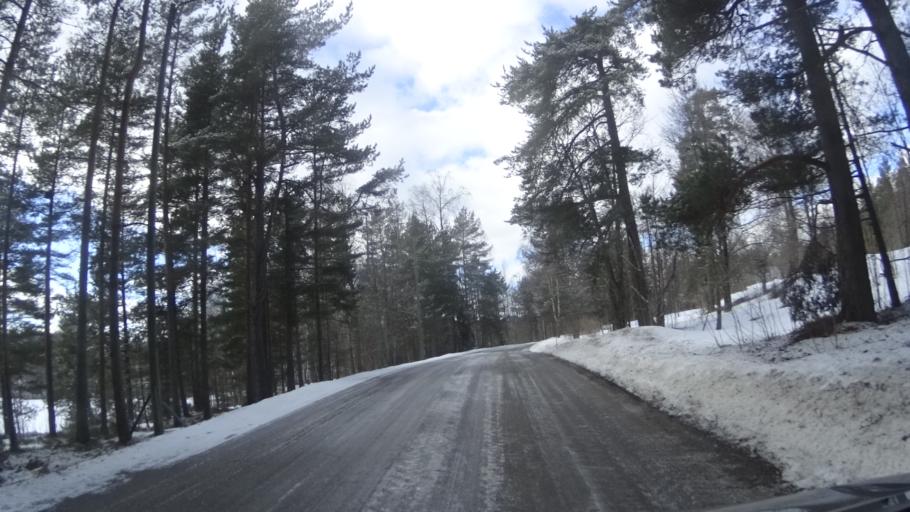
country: FI
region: Uusimaa
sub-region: Helsinki
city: Vantaa
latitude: 60.2544
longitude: 25.1620
